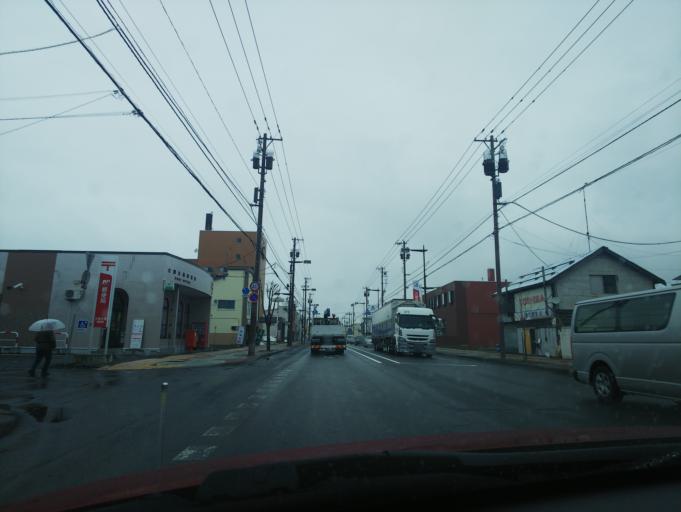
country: JP
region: Hokkaido
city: Nayoro
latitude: 44.1791
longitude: 142.3913
